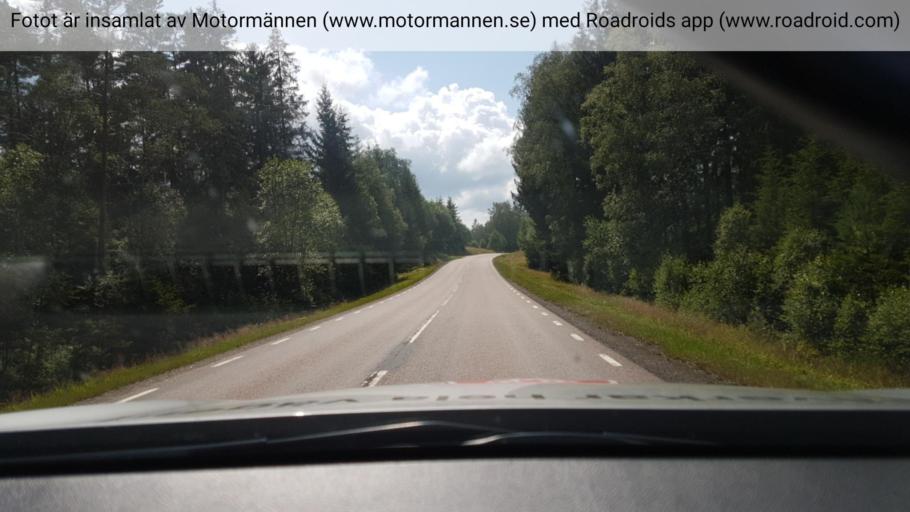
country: SE
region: Vaestra Goetaland
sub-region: Marks Kommun
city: Fritsla
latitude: 57.4920
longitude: 12.8910
